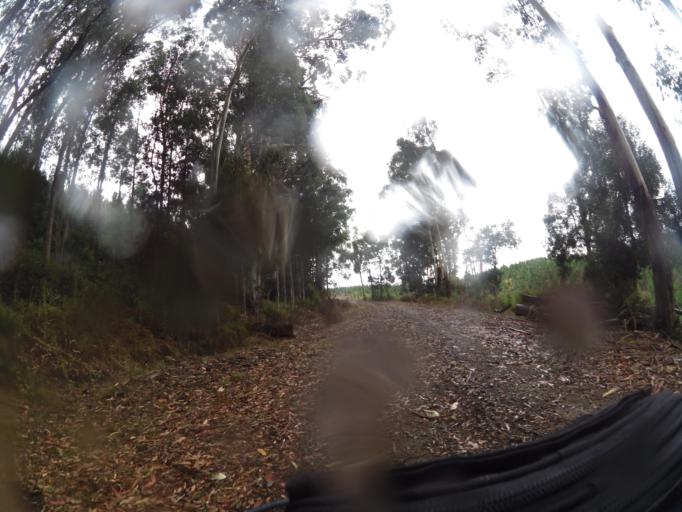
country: AU
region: New South Wales
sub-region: Greater Hume Shire
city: Holbrook
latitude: -36.2179
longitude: 147.5662
